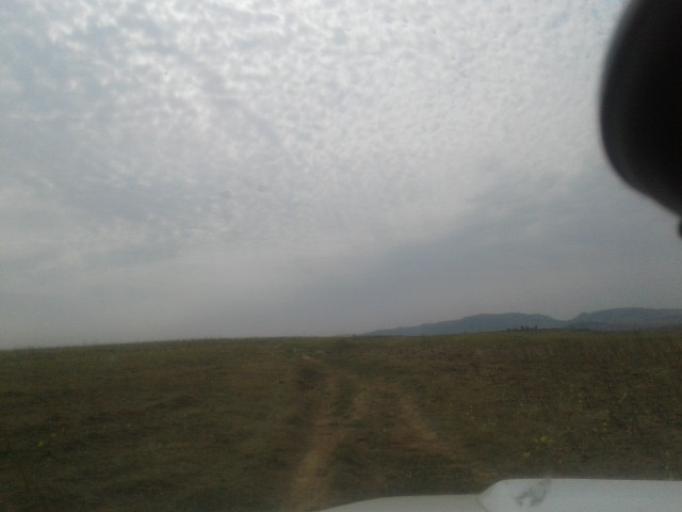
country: LS
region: Berea
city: Teyateyaneng
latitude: -29.1117
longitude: 27.9083
